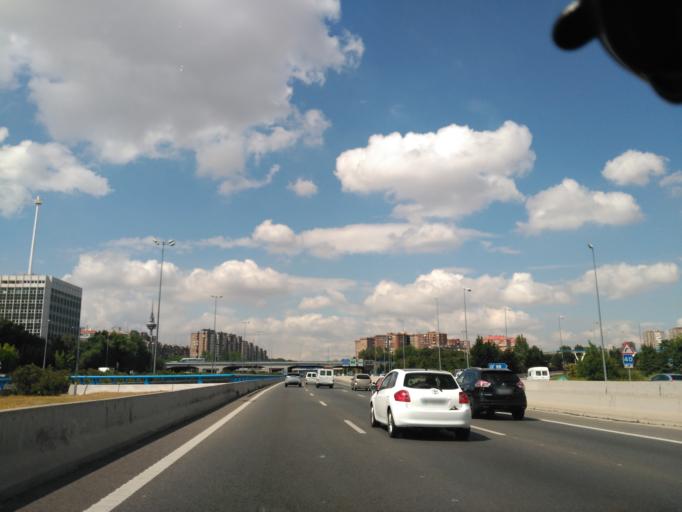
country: ES
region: Madrid
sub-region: Provincia de Madrid
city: Puente de Vallecas
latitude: 40.4037
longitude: -3.6664
